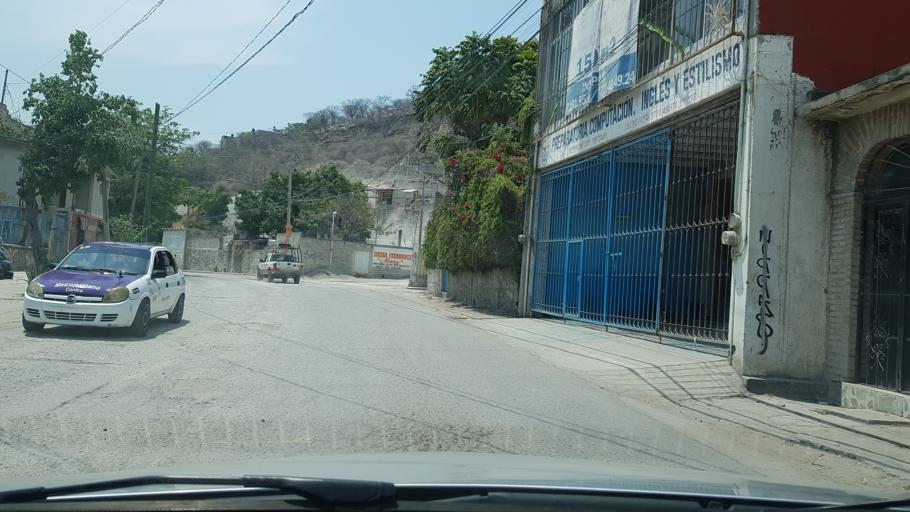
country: MX
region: Morelos
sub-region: Jiutepec
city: Calera Chica
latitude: 18.8573
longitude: -99.1803
